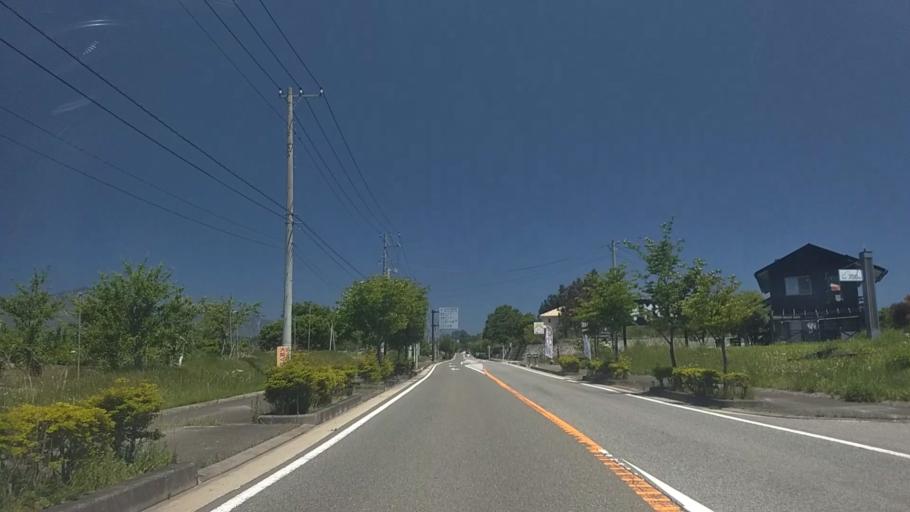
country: JP
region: Yamanashi
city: Nirasaki
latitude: 35.8313
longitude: 138.4298
